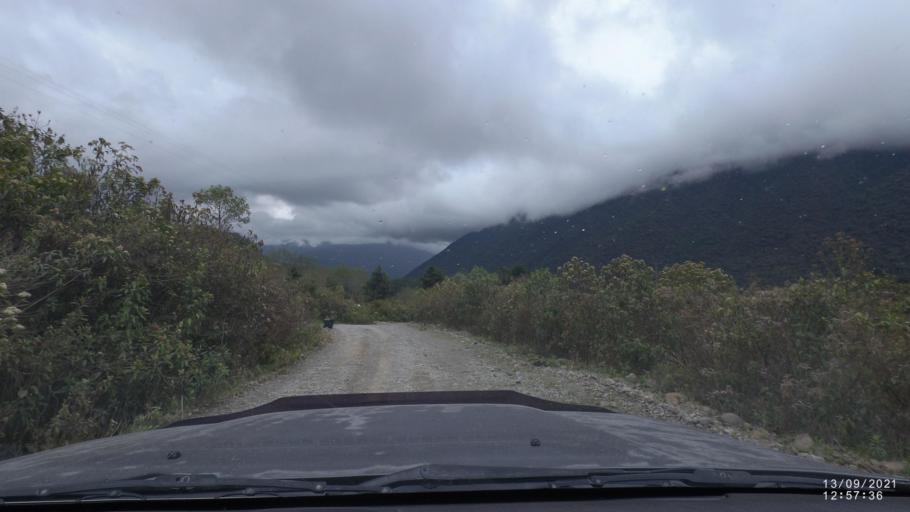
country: BO
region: Cochabamba
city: Colomi
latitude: -17.2403
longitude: -65.8179
